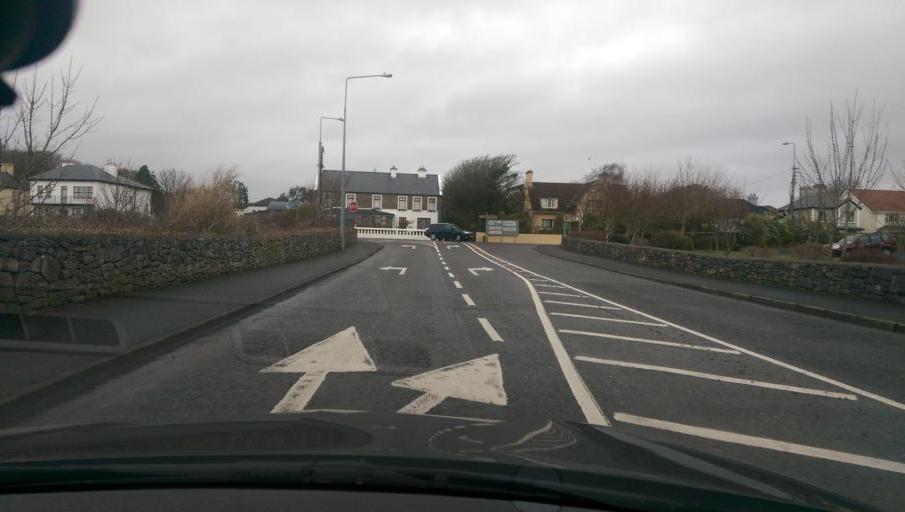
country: IE
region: Connaught
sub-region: County Galway
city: Bearna
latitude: 53.2604
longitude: -9.1081
